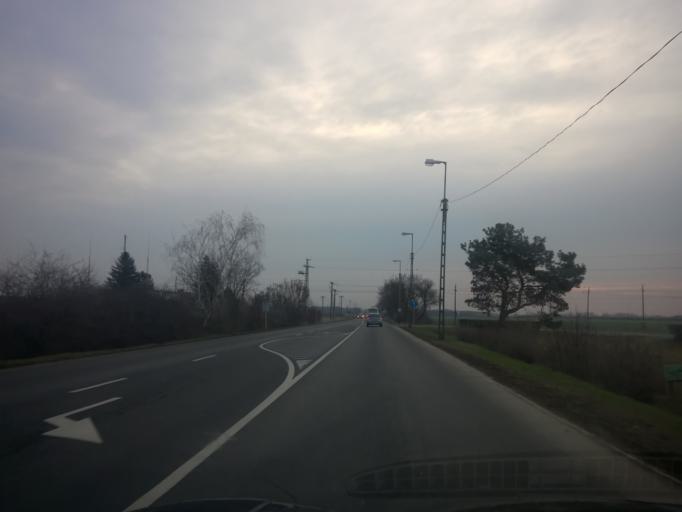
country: HU
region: Baranya
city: Szigetvar
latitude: 46.0488
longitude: 17.8254
